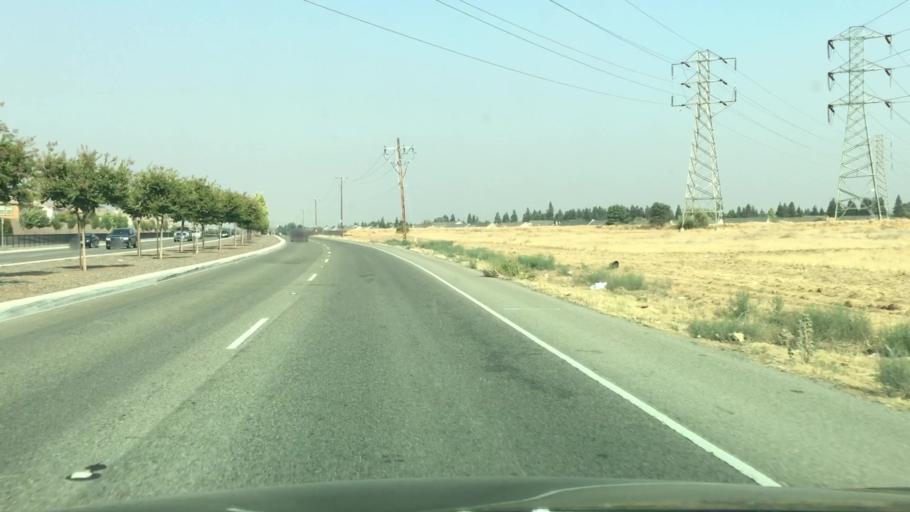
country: US
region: California
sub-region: Fresno County
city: Biola
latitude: 36.8368
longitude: -119.9002
